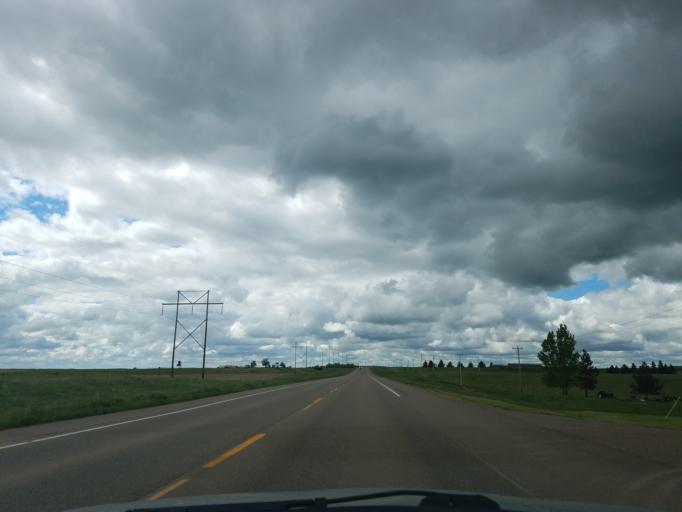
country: US
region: North Dakota
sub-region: McKenzie County
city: Watford City
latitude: 47.4330
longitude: -103.2481
